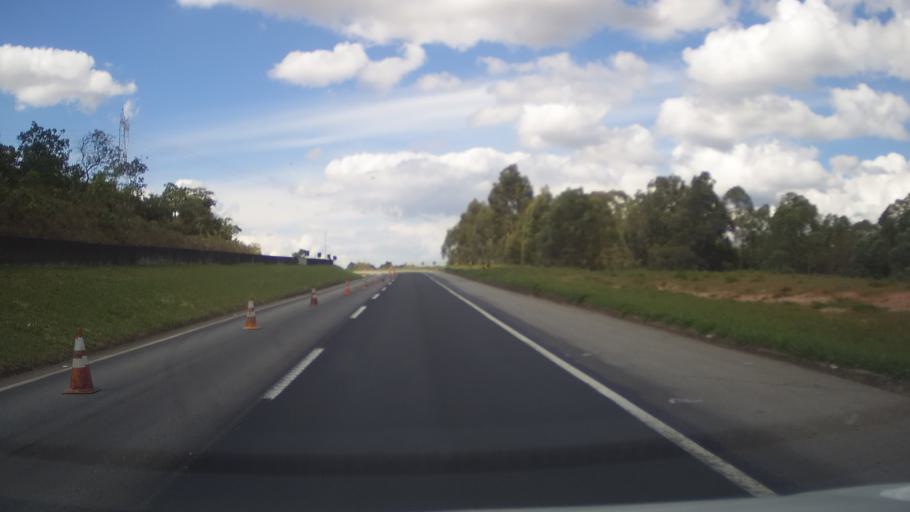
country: BR
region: Minas Gerais
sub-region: Santo Antonio Do Amparo
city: Santo Antonio do Amparo
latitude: -20.8404
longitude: -44.8254
